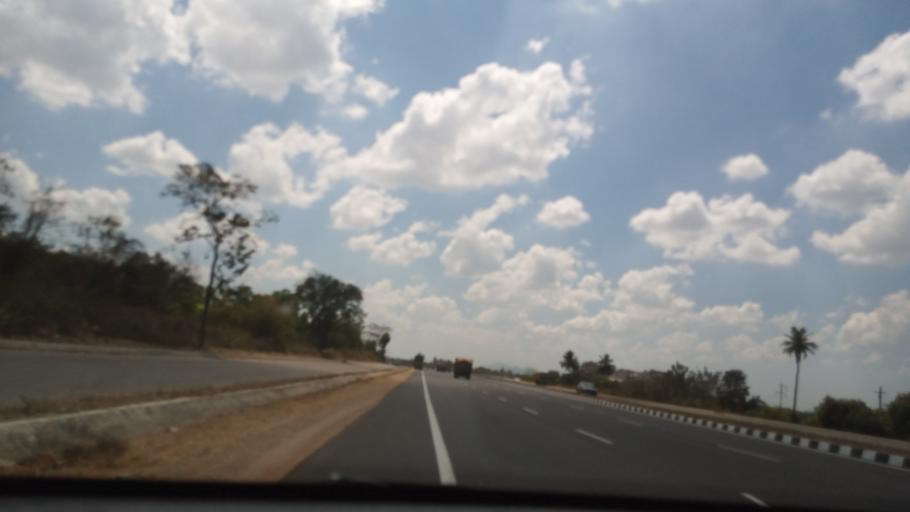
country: IN
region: Andhra Pradesh
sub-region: Chittoor
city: Pakala
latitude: 13.4432
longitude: 79.1482
